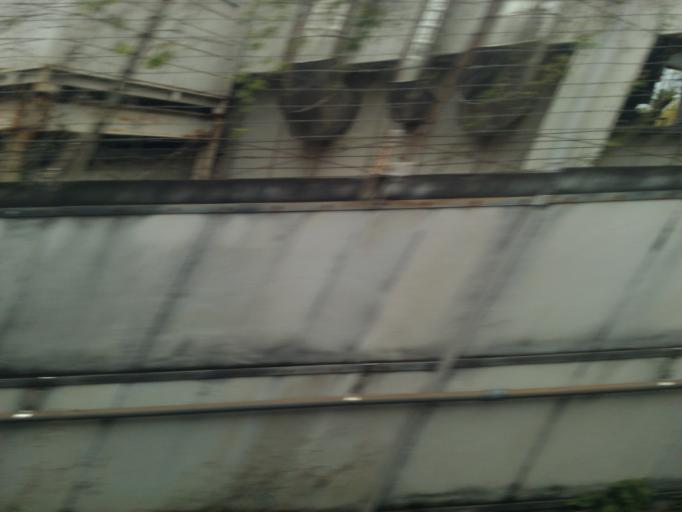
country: JP
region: Kanagawa
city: Yokohama
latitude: 35.4859
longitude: 139.5844
